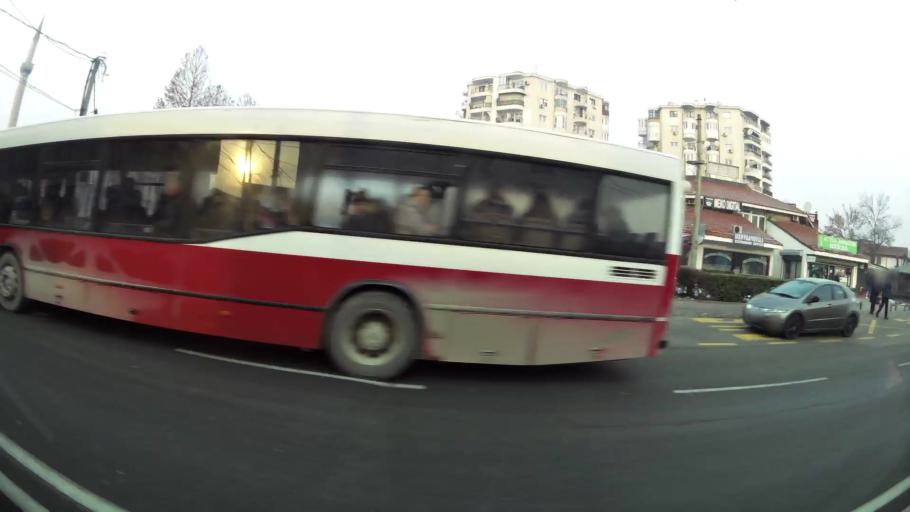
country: MK
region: Cair
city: Cair
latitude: 42.0084
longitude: 21.4433
